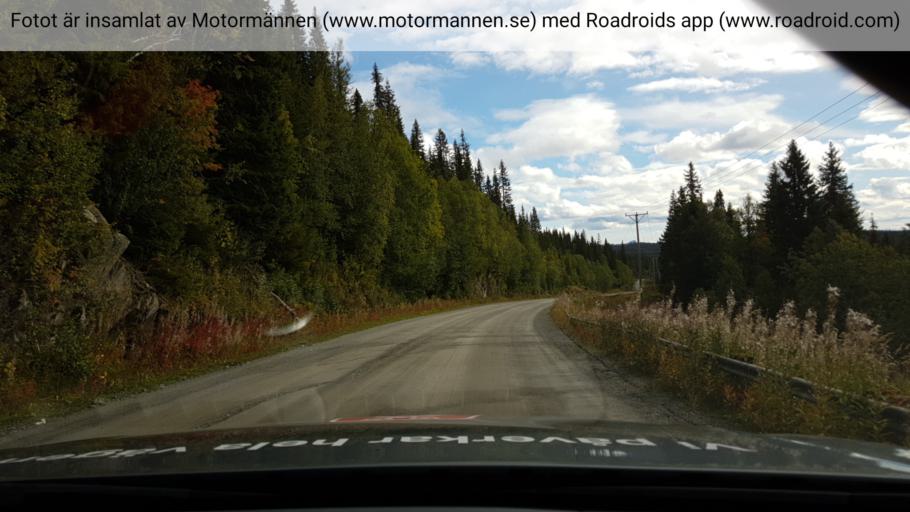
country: SE
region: Jaemtland
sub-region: Are Kommun
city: Are
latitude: 63.6975
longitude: 12.7843
